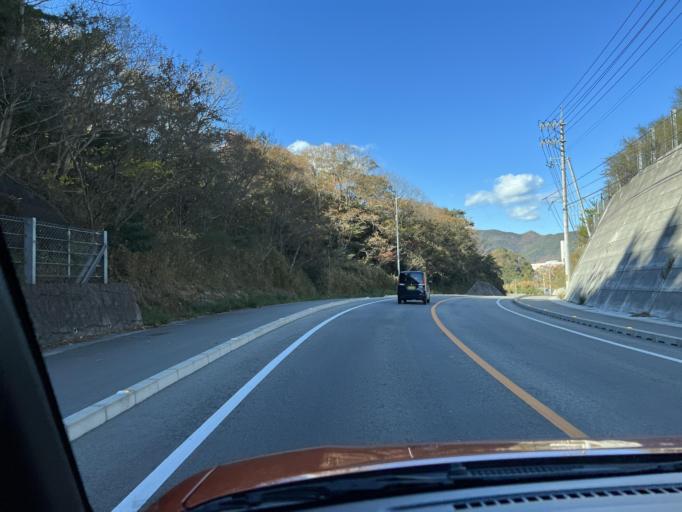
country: JP
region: Kagawa
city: Tonosho
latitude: 34.4739
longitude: 134.2546
